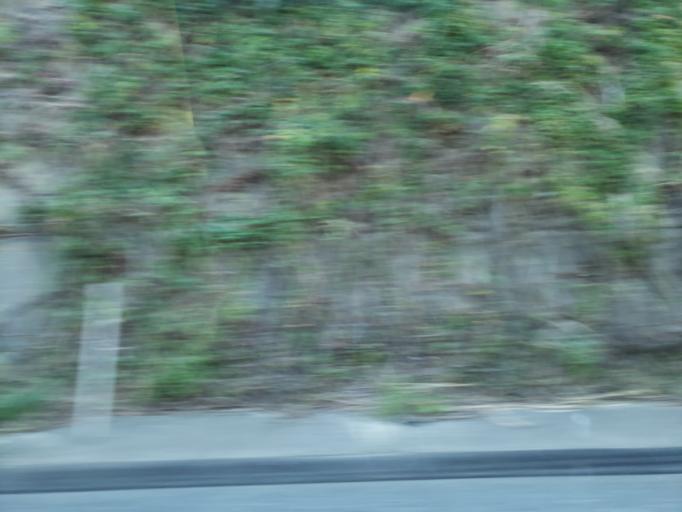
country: JP
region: Tokushima
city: Ishii
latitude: 34.1427
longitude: 134.4372
